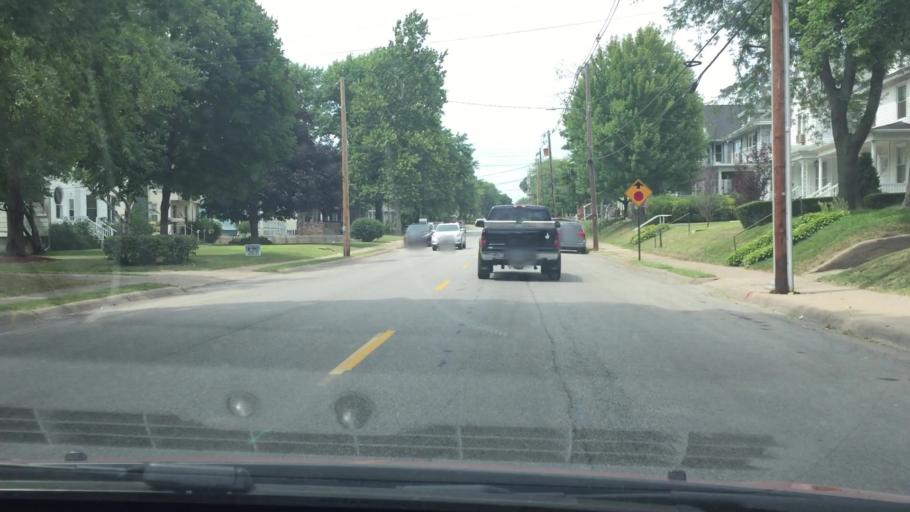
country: US
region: Iowa
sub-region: Muscatine County
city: Muscatine
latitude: 41.4346
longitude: -91.0531
